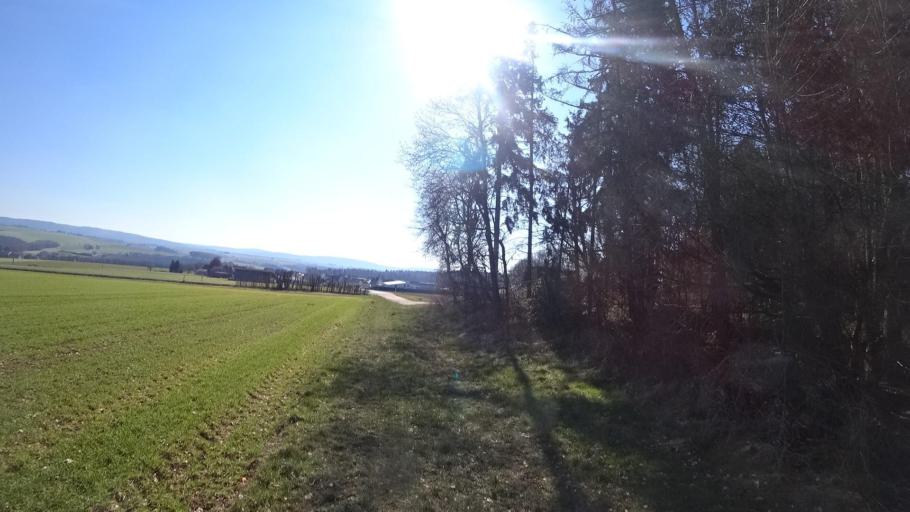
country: DE
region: Rheinland-Pfalz
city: Schonborn
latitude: 49.9504
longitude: 7.4714
